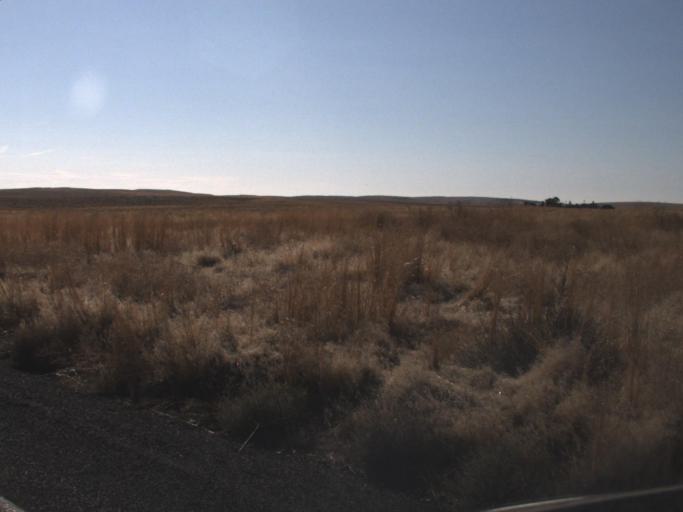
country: US
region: Washington
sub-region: Franklin County
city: Connell
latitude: 46.7360
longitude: -118.5478
